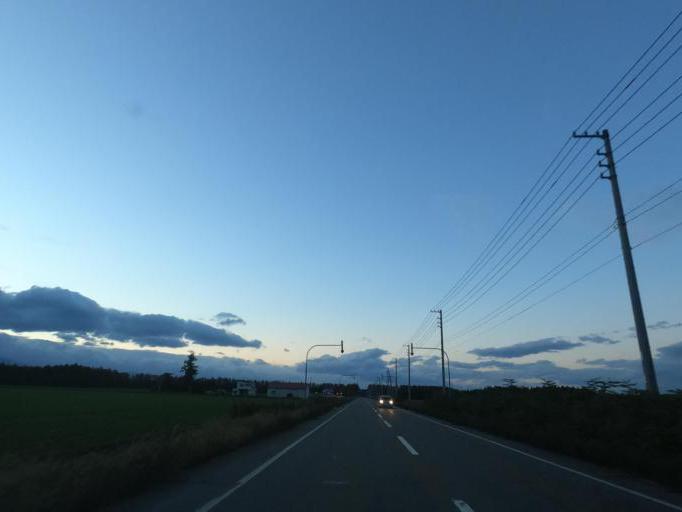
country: JP
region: Hokkaido
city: Obihiro
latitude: 42.6680
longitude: 143.1738
